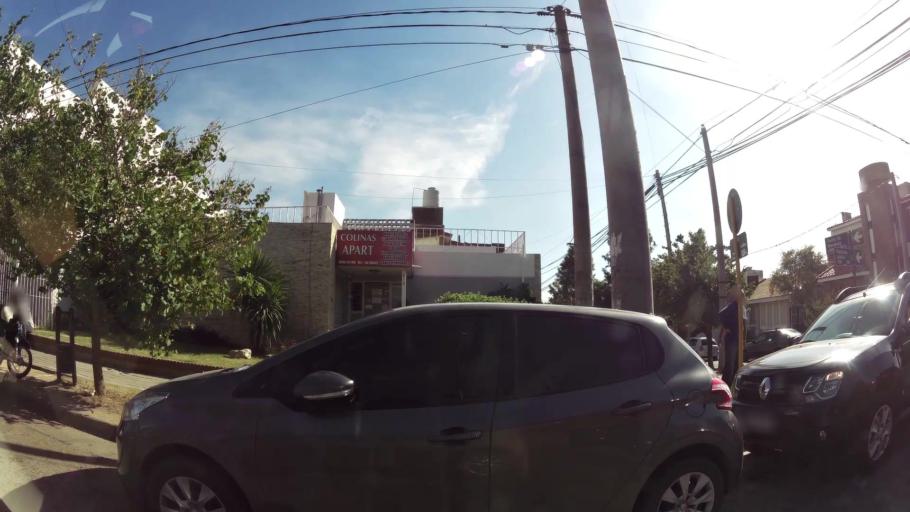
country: AR
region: Cordoba
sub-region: Departamento de Capital
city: Cordoba
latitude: -31.4412
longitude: -64.2072
